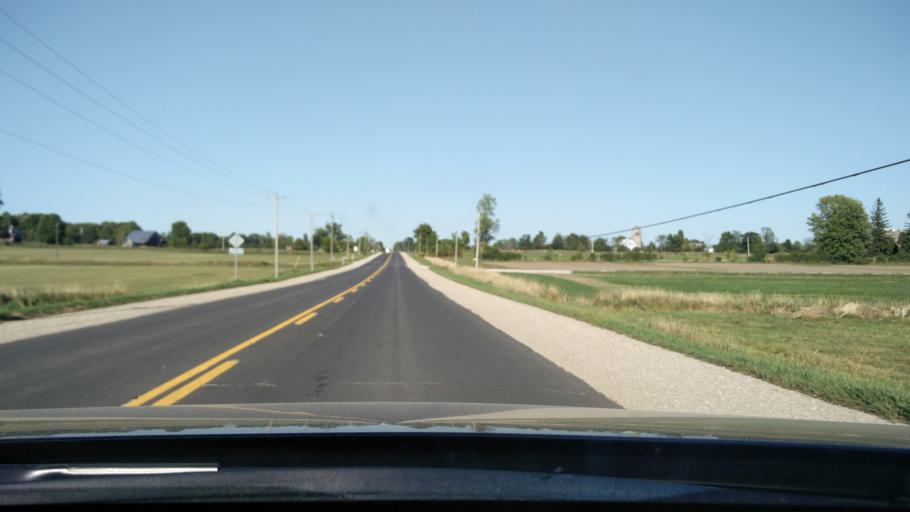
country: CA
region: Ontario
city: Perth
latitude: 44.8658
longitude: -76.2824
